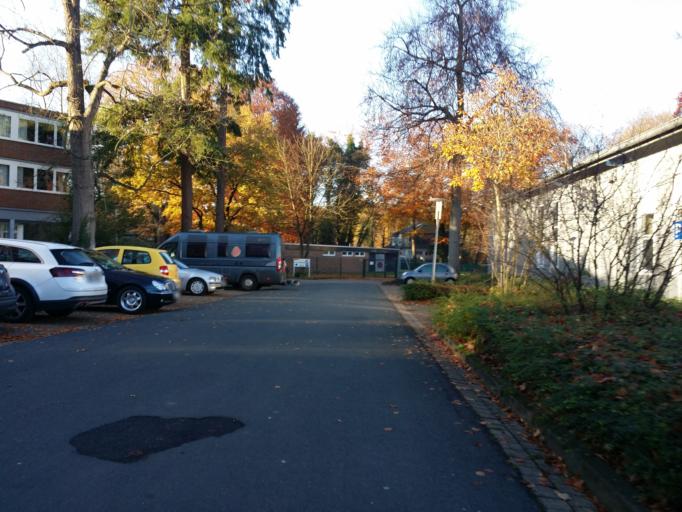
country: DE
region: Lower Saxony
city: Rotenburg
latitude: 53.0972
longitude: 9.3739
